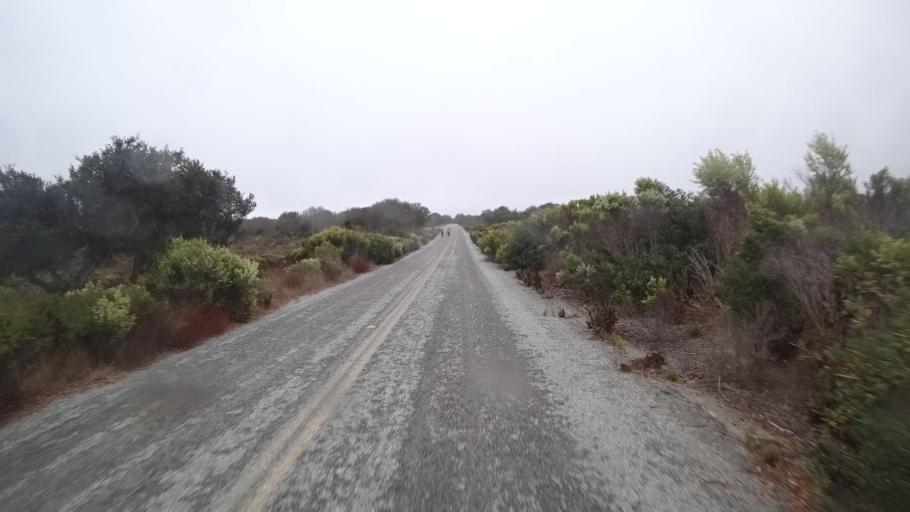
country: US
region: California
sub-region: Monterey County
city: Boronda
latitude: 36.6434
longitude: -121.7321
